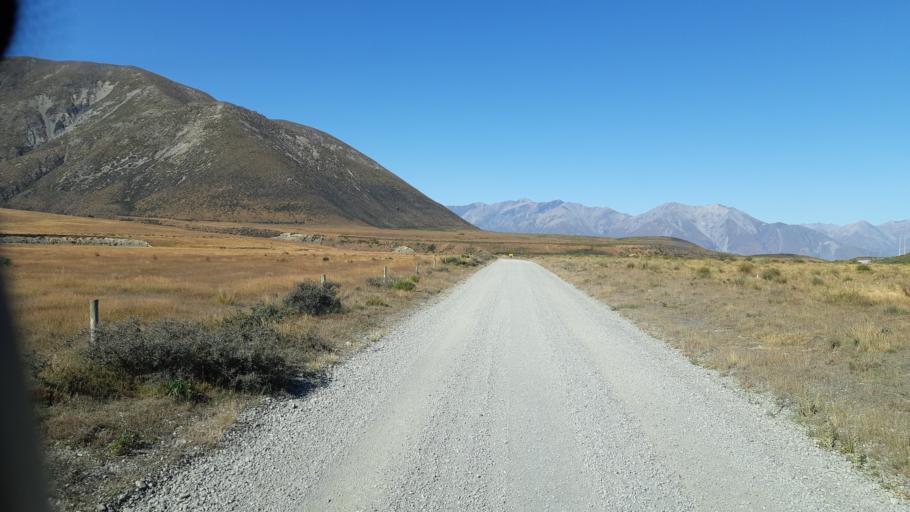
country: NZ
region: Canterbury
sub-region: Ashburton District
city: Methven
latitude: -43.3296
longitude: 171.6780
